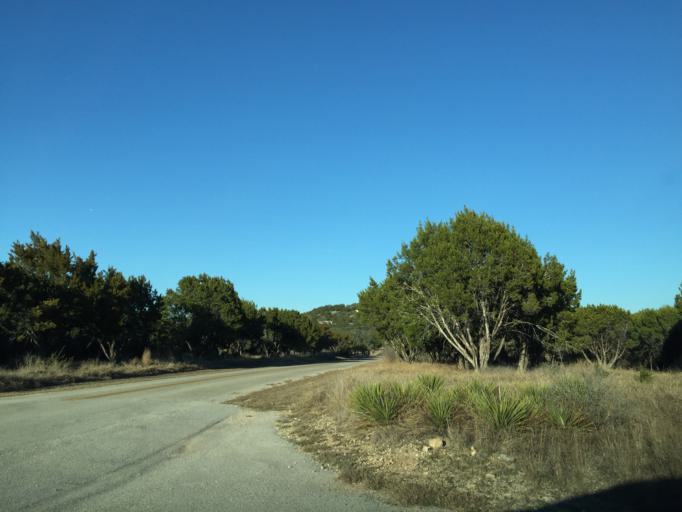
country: US
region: Texas
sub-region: Travis County
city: Briarcliff
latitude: 30.5072
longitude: -98.1047
